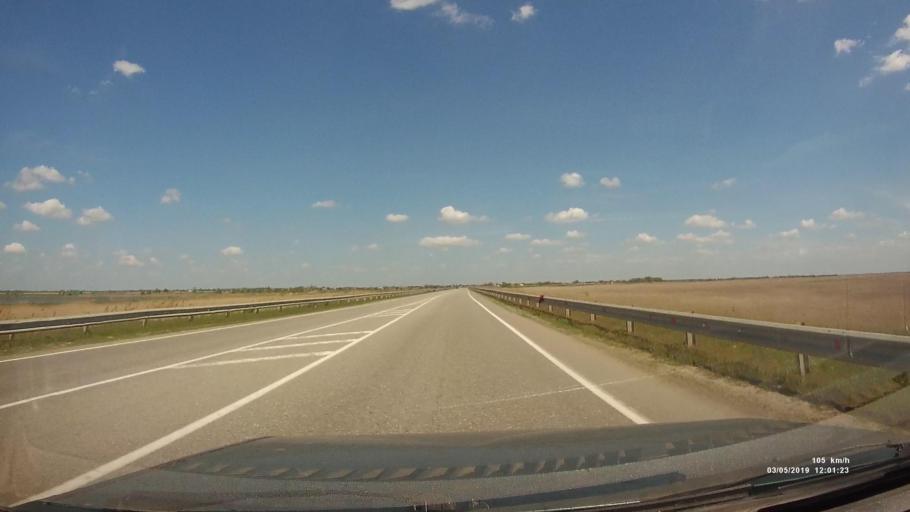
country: RU
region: Rostov
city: Bagayevskaya
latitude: 47.2621
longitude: 40.3501
